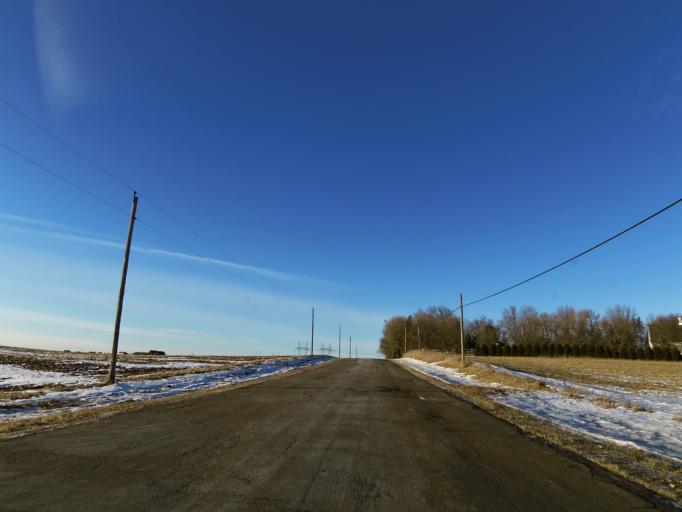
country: US
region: Minnesota
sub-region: Washington County
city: Cottage Grove
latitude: 44.8105
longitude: -92.8788
